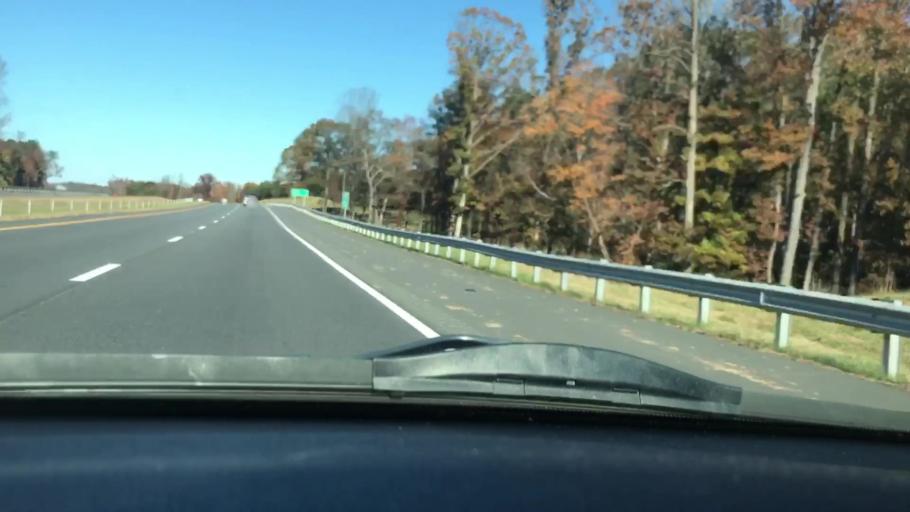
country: US
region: North Carolina
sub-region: Guilford County
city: Summerfield
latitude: 36.2147
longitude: -79.9180
